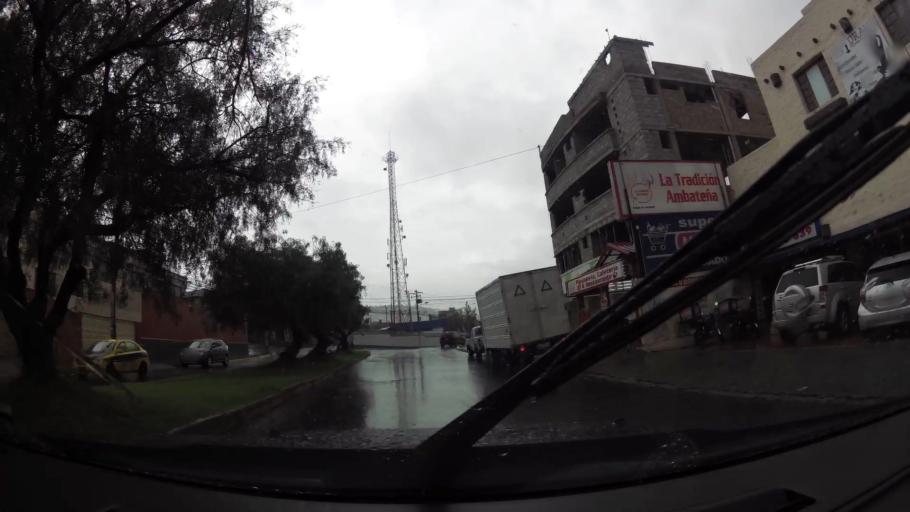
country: EC
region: Pichincha
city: Quito
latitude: -0.1047
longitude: -78.5002
